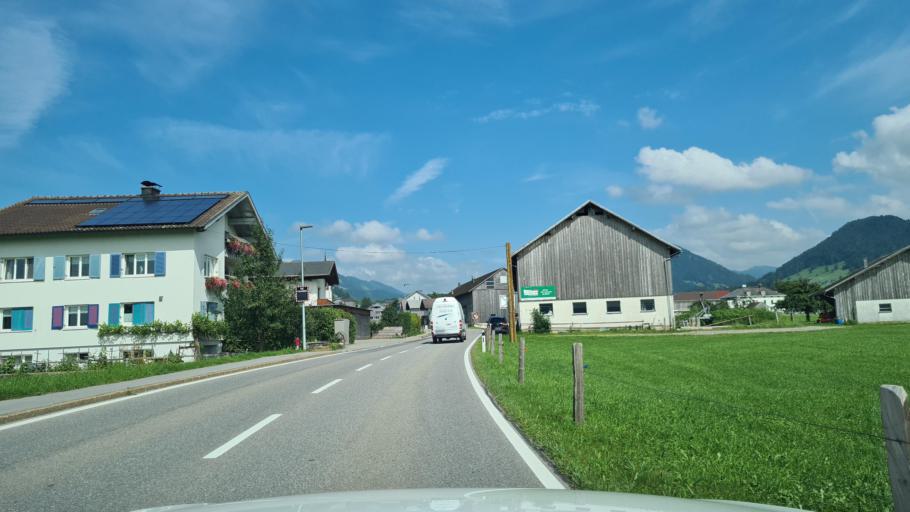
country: AT
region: Vorarlberg
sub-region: Politischer Bezirk Bregenz
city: Egg
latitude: 47.4485
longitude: 9.9139
